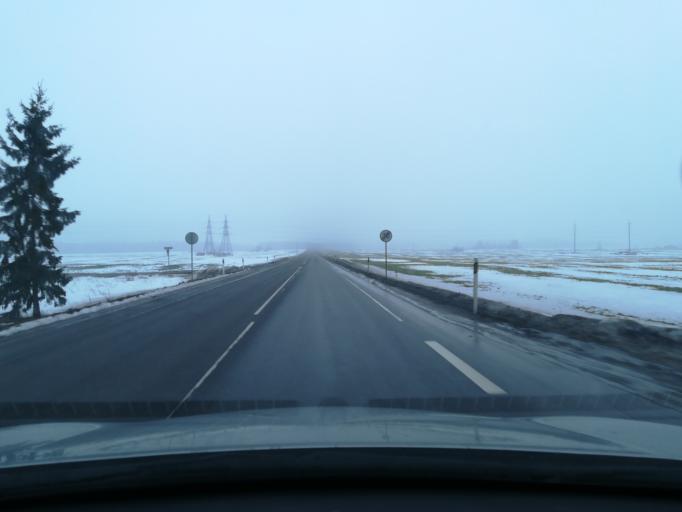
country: EE
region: Harju
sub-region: Raasiku vald
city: Arukula
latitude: 59.3628
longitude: 25.0469
